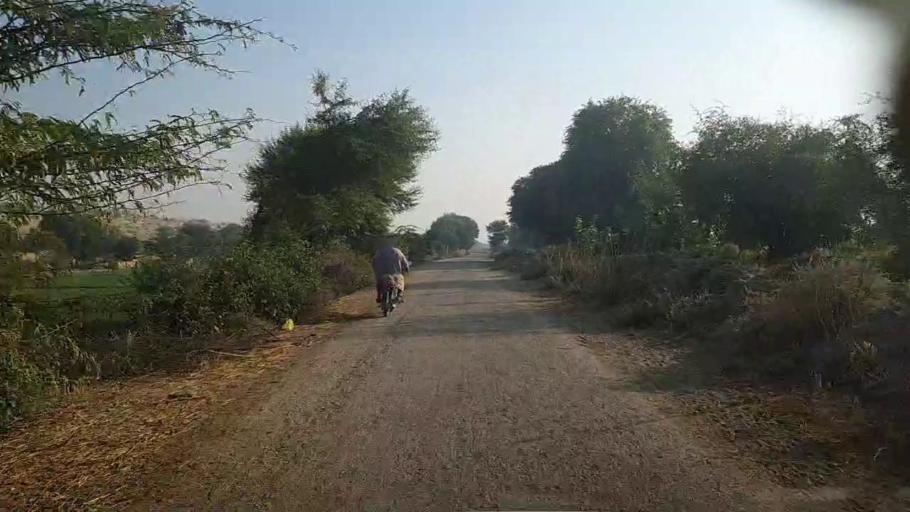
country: PK
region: Sindh
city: Karaundi
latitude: 26.7655
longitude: 68.4745
